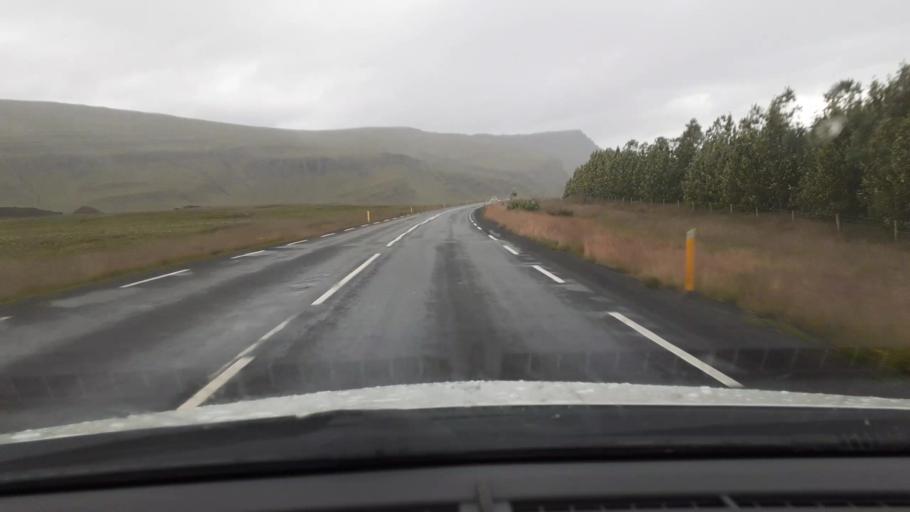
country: IS
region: West
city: Borgarnes
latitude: 64.3711
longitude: -21.8598
